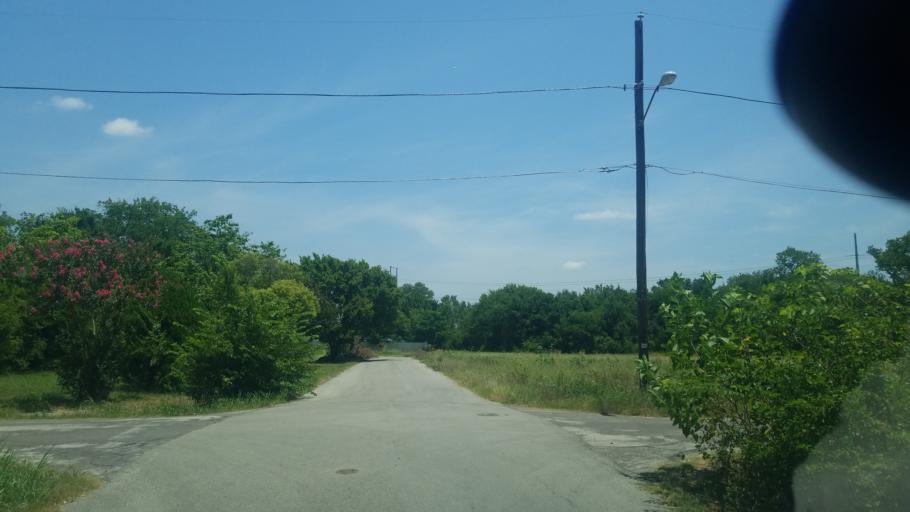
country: US
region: Texas
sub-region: Dallas County
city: Dallas
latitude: 32.7422
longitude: -96.7841
